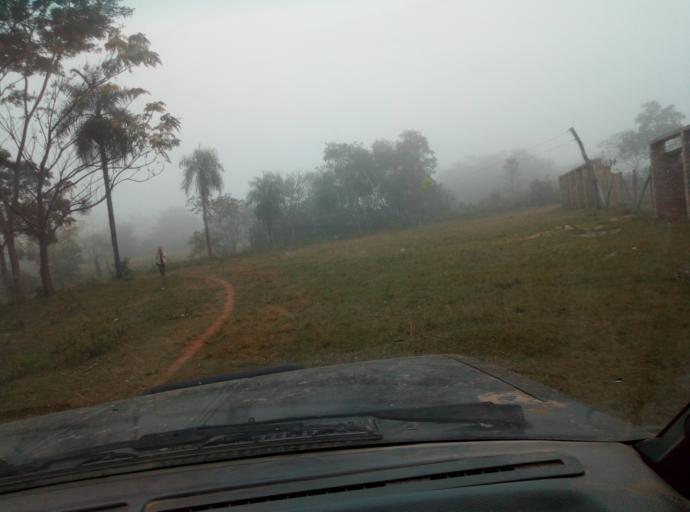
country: PY
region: Caaguazu
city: Doctor Cecilio Baez
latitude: -25.1553
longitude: -56.2492
